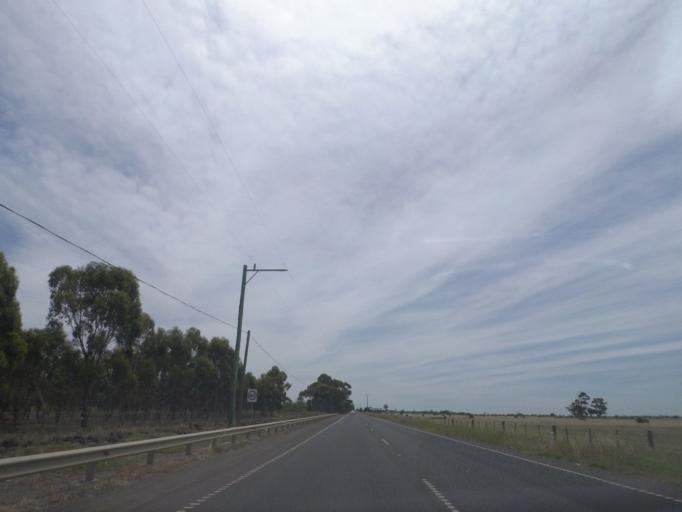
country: AU
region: Victoria
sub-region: Wyndham
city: Truganina
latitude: -37.8041
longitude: 144.6960
